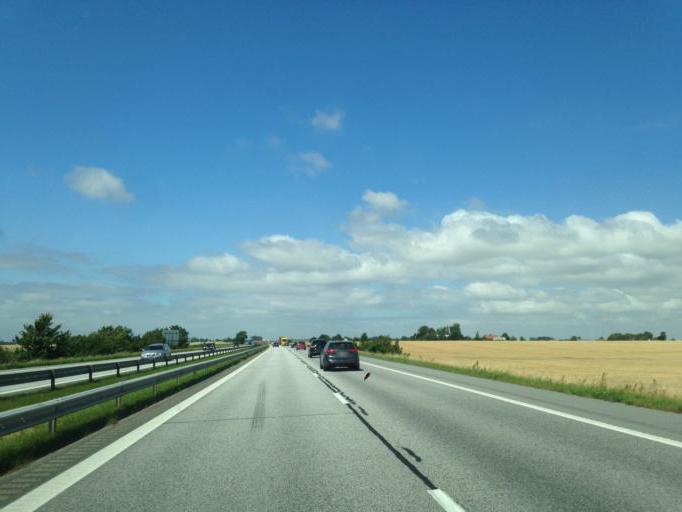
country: SE
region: Skane
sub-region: Vellinge Kommun
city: Vellinge
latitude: 55.4940
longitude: 13.0207
